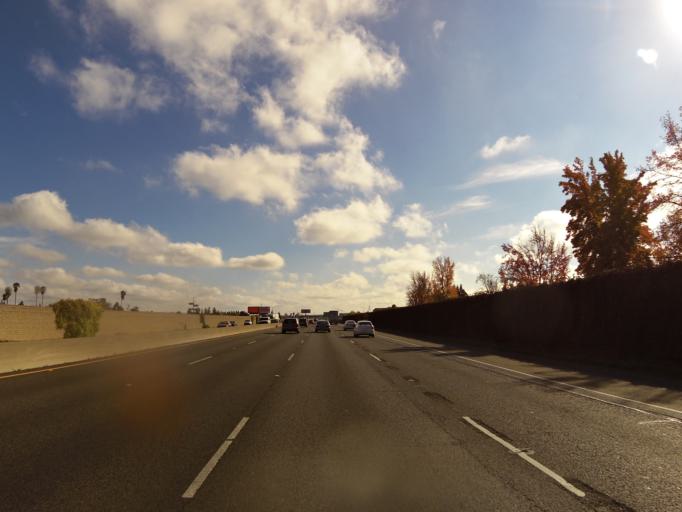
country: US
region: California
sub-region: Sacramento County
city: Florin
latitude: 38.4809
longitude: -121.4300
